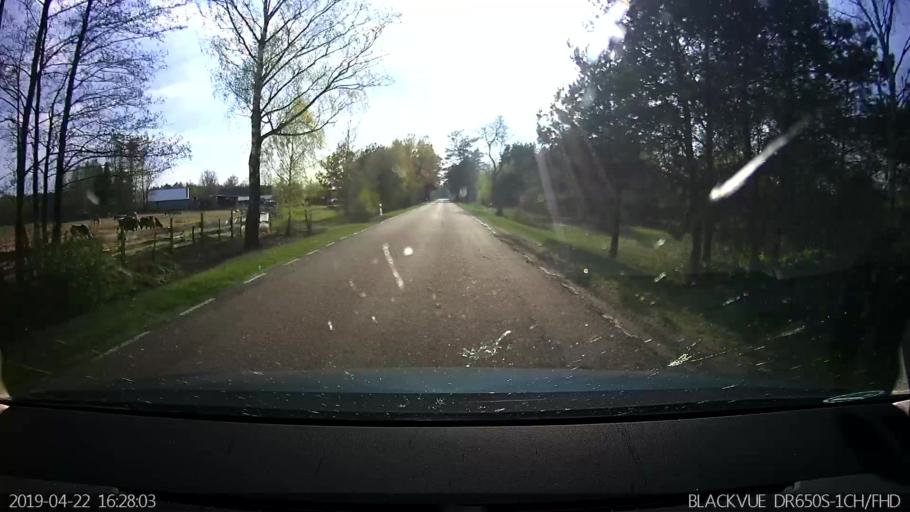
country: PL
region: Podlasie
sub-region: Powiat siemiatycki
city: Milejczyce
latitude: 52.5416
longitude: 23.1883
